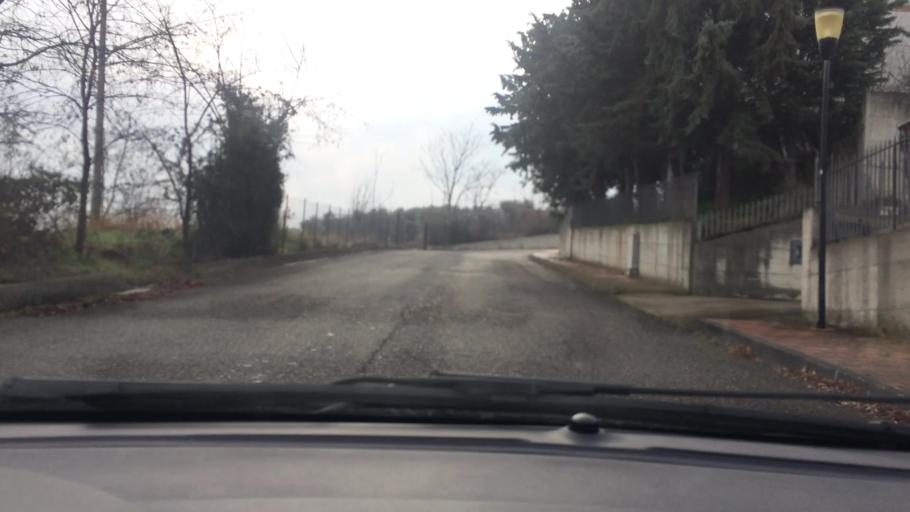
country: IT
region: Basilicate
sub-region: Provincia di Matera
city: San Mauro Forte
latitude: 40.4907
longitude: 16.2423
